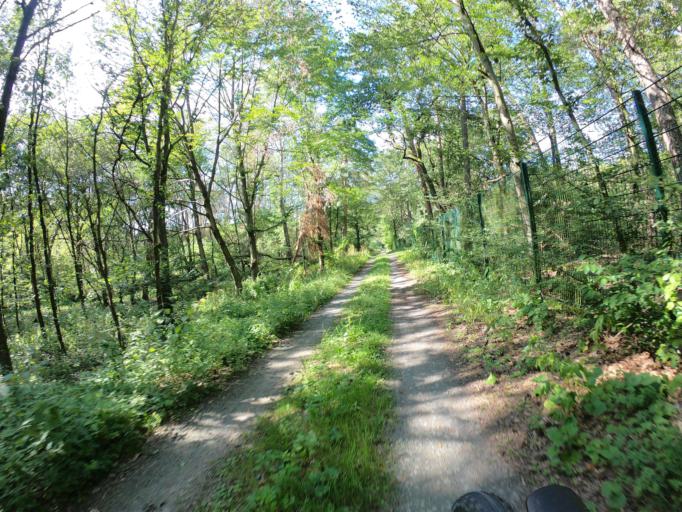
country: DE
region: Hesse
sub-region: Regierungsbezirk Darmstadt
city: Erzhausen
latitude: 49.9871
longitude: 8.6295
